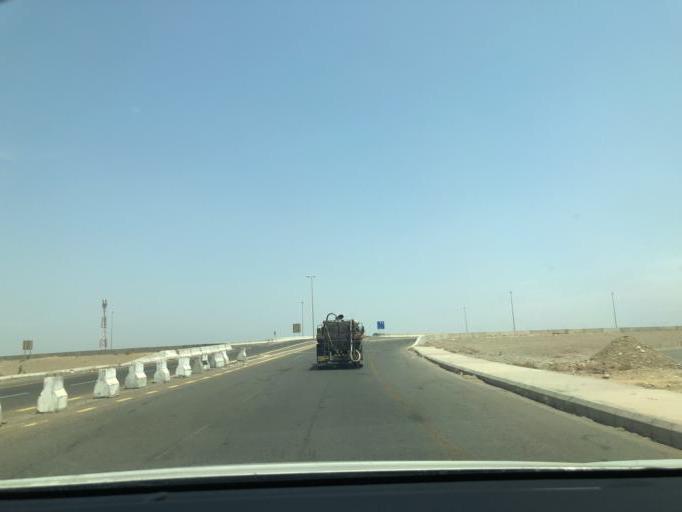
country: SA
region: Makkah
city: Rabigh
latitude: 22.2750
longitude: 39.1234
